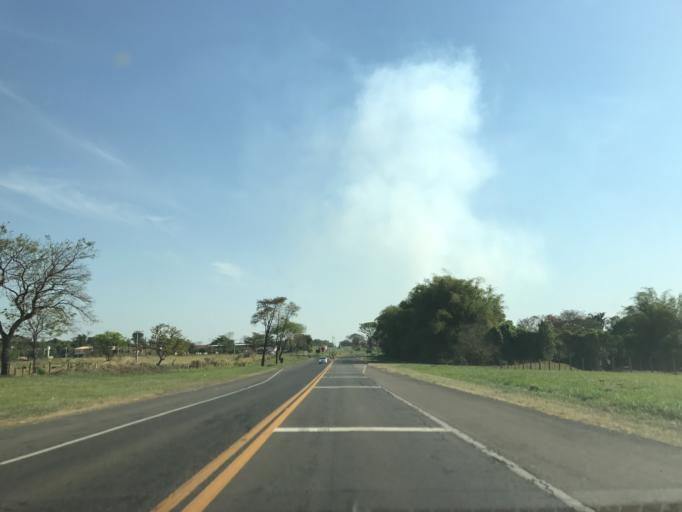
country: BR
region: Sao Paulo
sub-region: Penapolis
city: Penapolis
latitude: -21.3827
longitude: -50.0920
